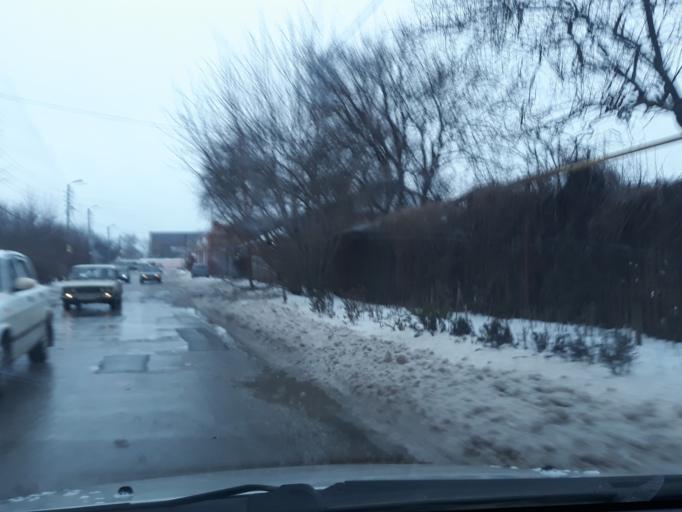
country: RU
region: Rostov
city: Taganrog
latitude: 47.2401
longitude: 38.8692
